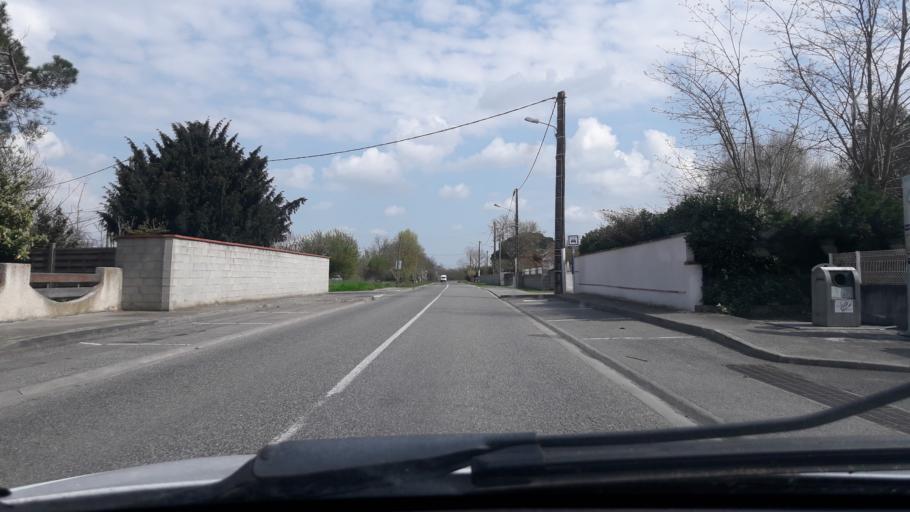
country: FR
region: Midi-Pyrenees
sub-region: Departement de la Haute-Garonne
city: Fonsorbes
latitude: 43.5035
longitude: 1.2596
